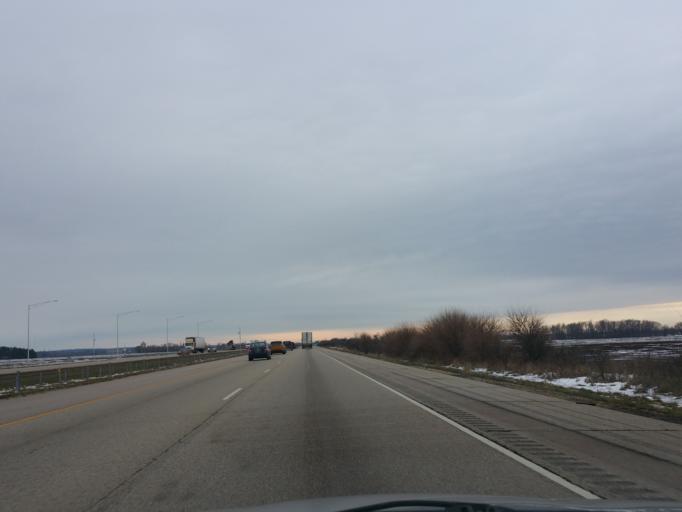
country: US
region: Wisconsin
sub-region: Rock County
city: Janesville
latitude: 42.5932
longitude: -88.9819
